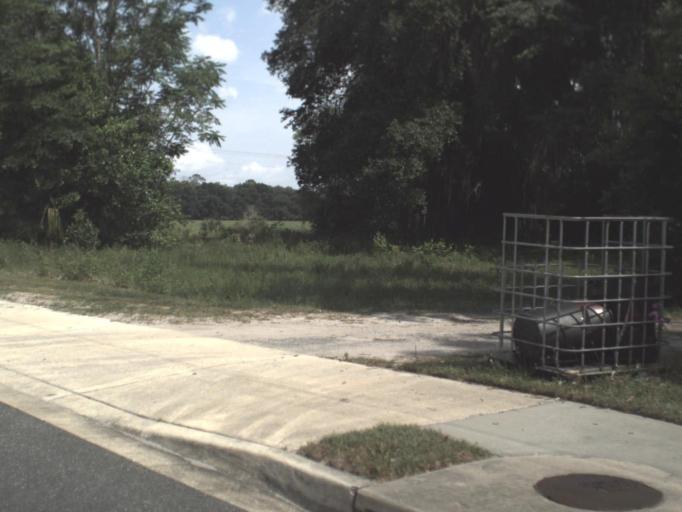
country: US
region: Florida
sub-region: Putnam County
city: Palatka
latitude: 29.6297
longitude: -81.7258
